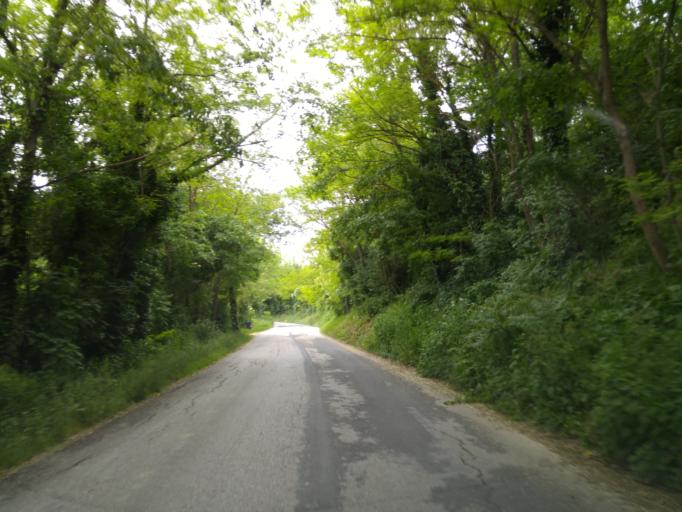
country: IT
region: The Marches
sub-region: Provincia di Pesaro e Urbino
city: Urbino
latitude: 43.7087
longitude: 12.6338
